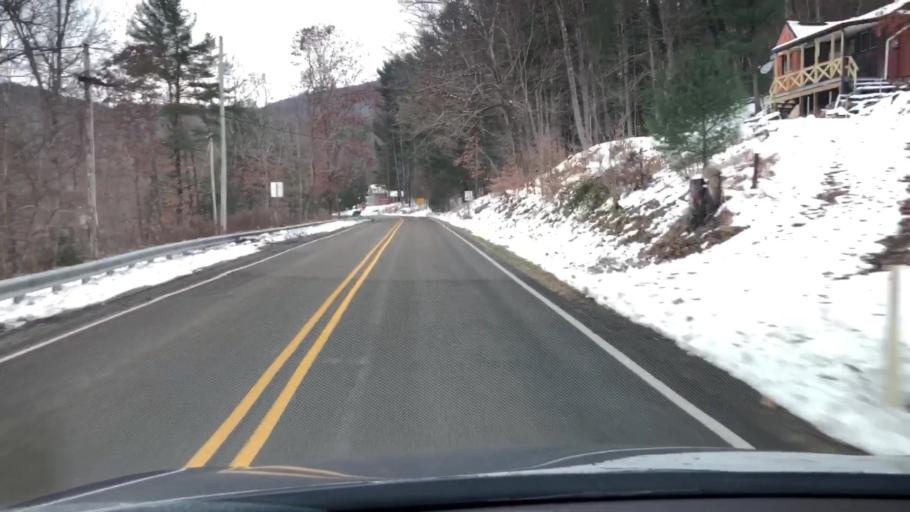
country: US
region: Pennsylvania
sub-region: Cameron County
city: Emporium
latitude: 41.3402
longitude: -78.3073
